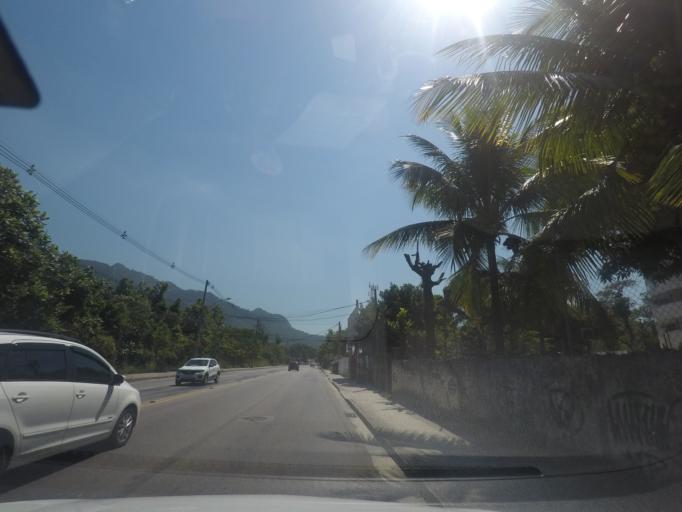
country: BR
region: Rio de Janeiro
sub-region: Nilopolis
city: Nilopolis
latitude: -22.9838
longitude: -43.4708
